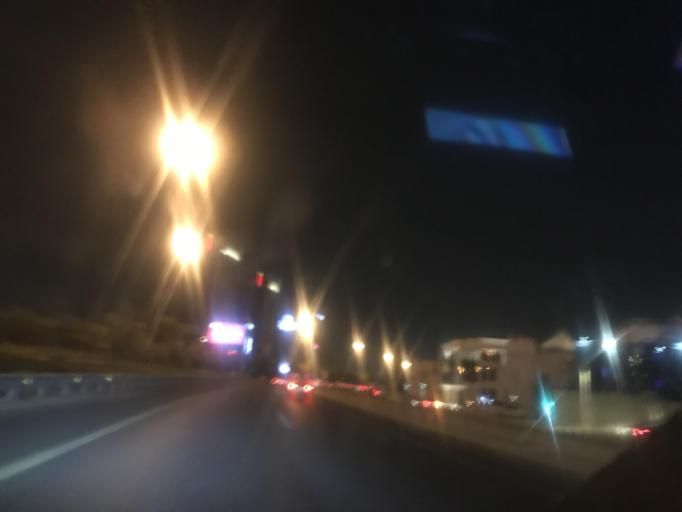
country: SA
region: Ar Riyad
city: Riyadh
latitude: 24.7615
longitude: 46.6509
